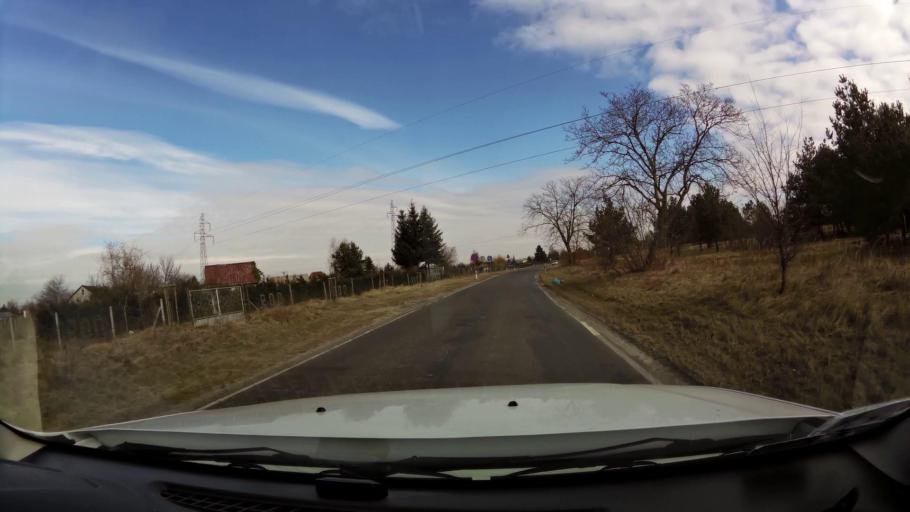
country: PL
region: West Pomeranian Voivodeship
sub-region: Powiat mysliborski
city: Debno
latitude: 52.7266
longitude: 14.6859
